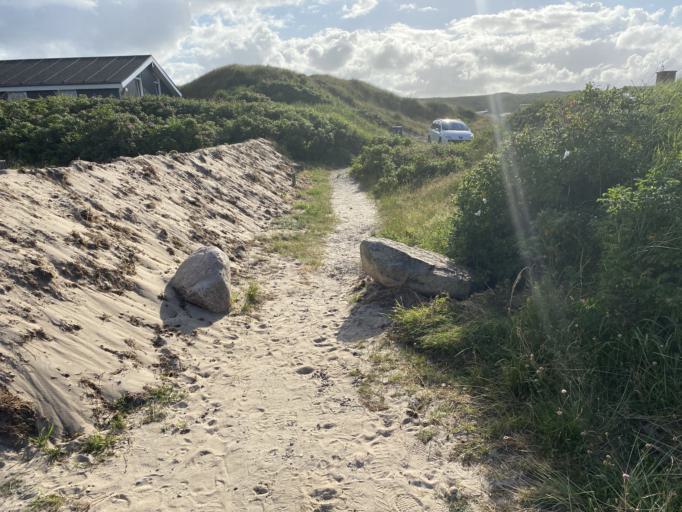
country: DK
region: Central Jutland
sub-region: Ringkobing-Skjern Kommune
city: Hvide Sande
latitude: 55.8620
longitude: 8.1650
